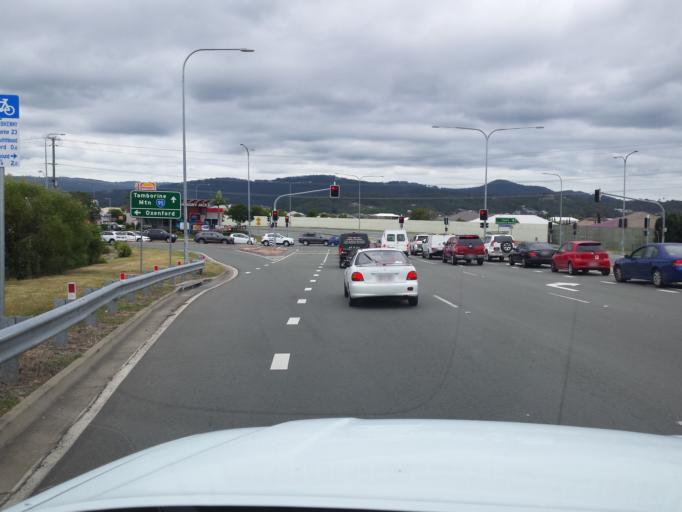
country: AU
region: Queensland
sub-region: Gold Coast
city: Oxenford
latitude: -27.8855
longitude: 153.3149
